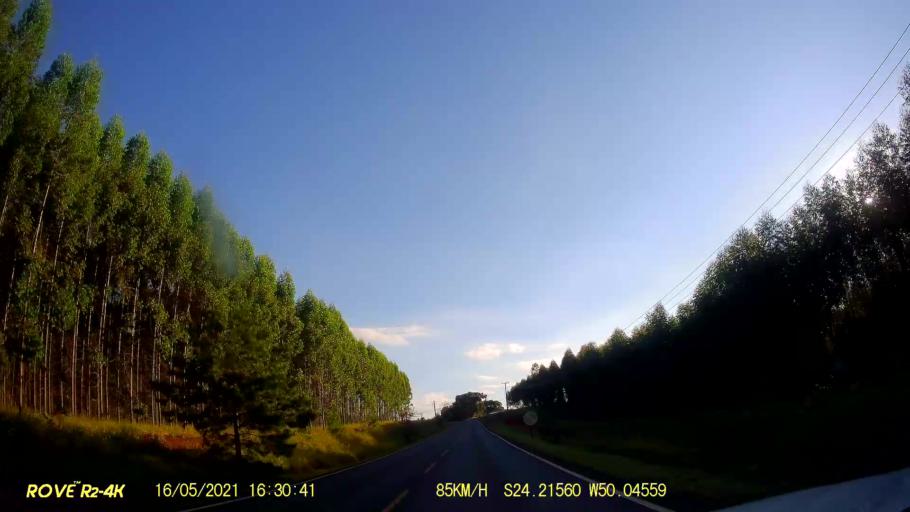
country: BR
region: Parana
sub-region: Pirai Do Sul
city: Pirai do Sul
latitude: -24.2157
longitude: -50.0458
